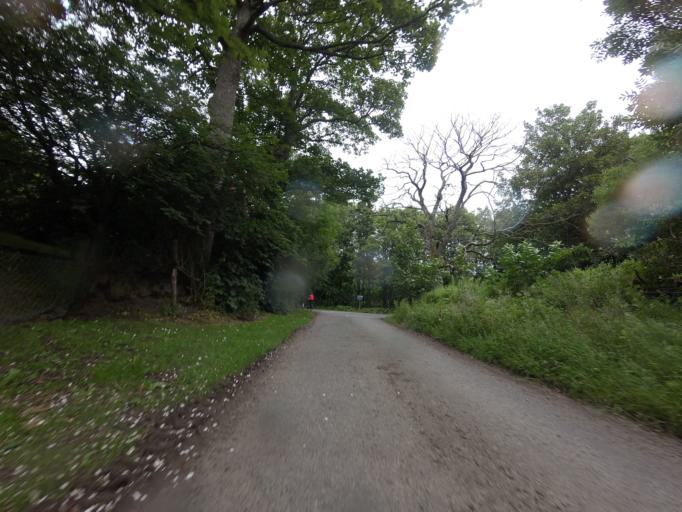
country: GB
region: Scotland
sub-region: Moray
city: Cullen
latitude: 57.6740
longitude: -2.7799
